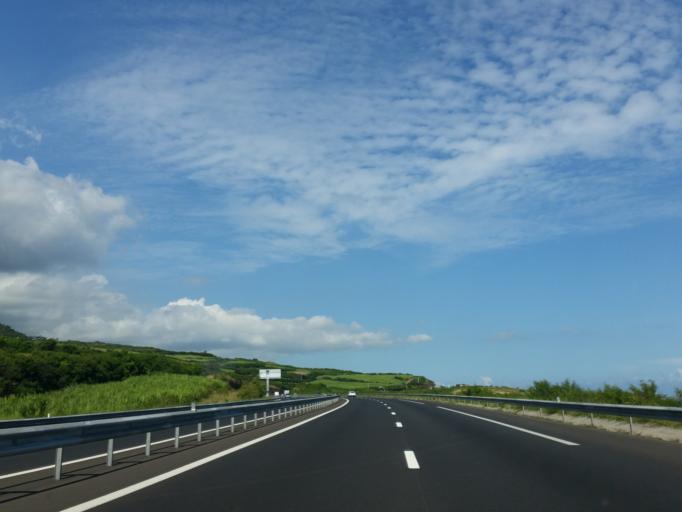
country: RE
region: Reunion
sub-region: Reunion
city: Trois-Bassins
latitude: -21.0763
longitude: 55.2521
